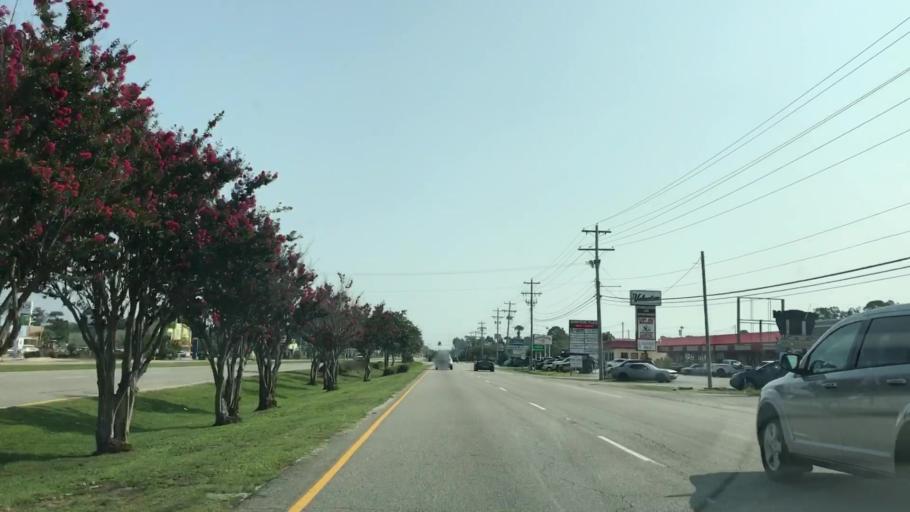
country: US
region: South Carolina
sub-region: Horry County
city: Surfside Beach
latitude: 33.6141
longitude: -78.9794
